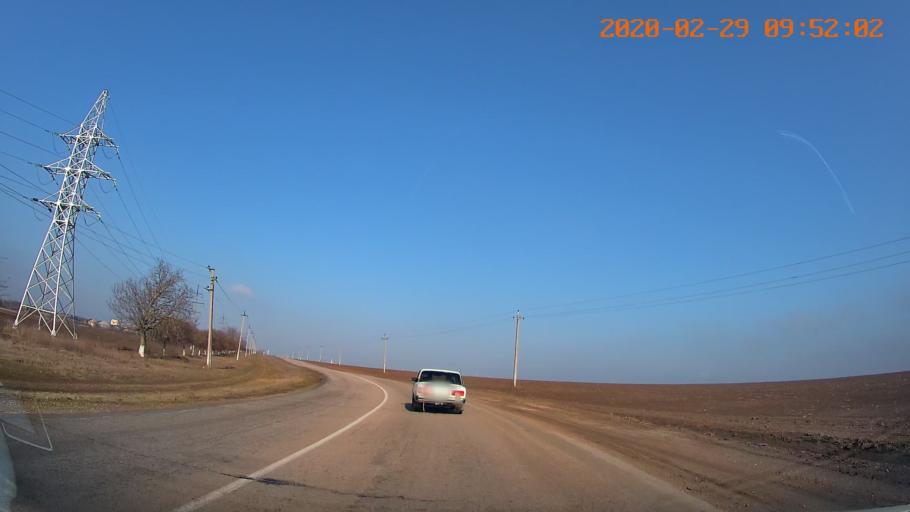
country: MD
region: Telenesti
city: Slobozia
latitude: 46.7135
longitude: 29.7344
